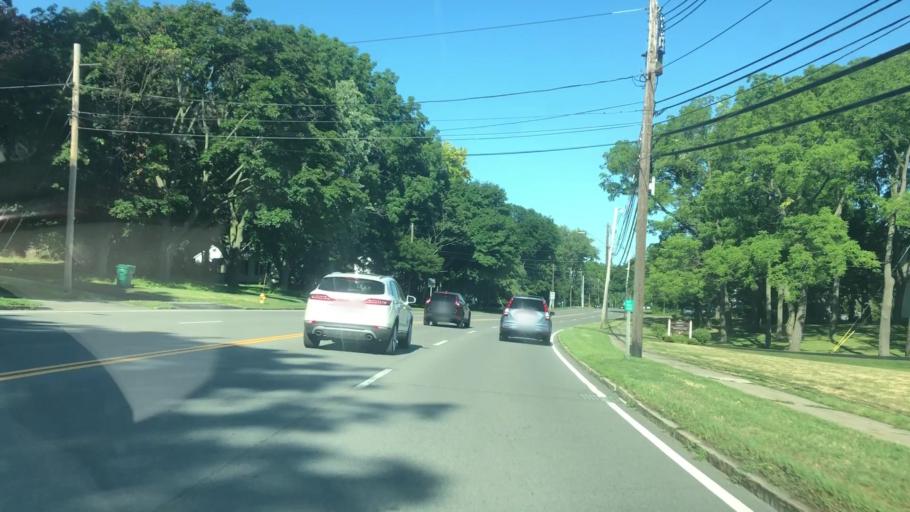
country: US
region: New York
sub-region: Monroe County
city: East Rochester
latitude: 43.1313
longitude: -77.4717
